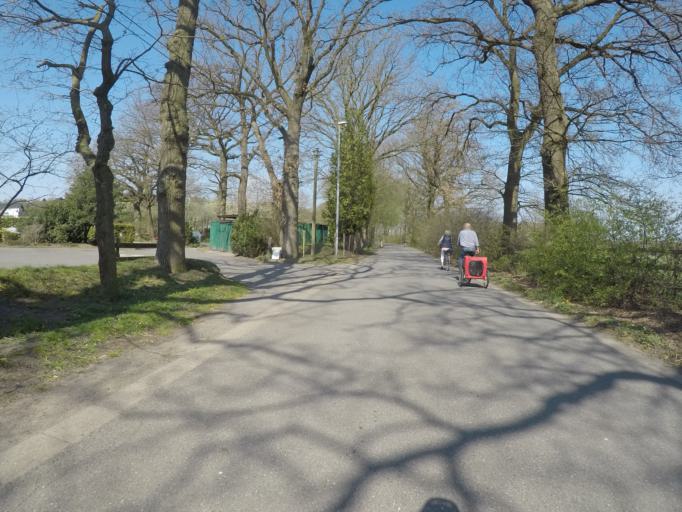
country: DE
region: Schleswig-Holstein
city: Rellingen
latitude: 53.6057
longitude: 9.8022
